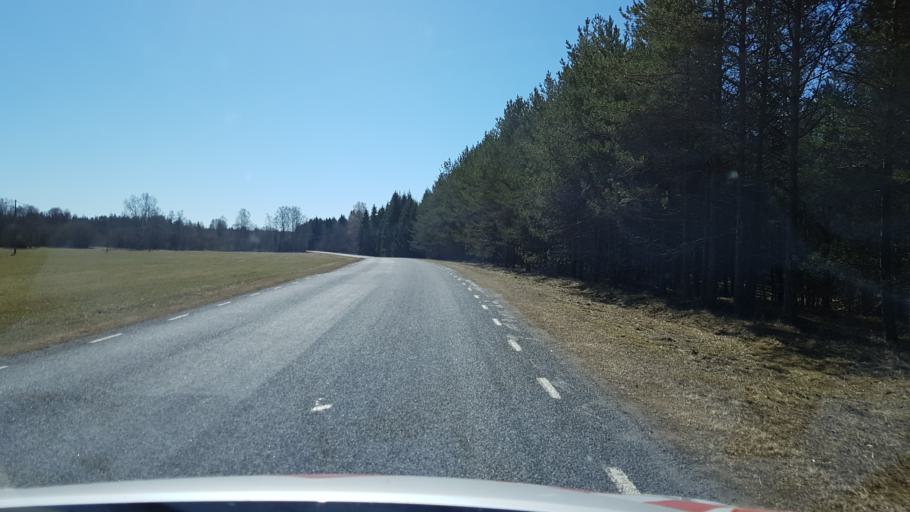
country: EE
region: Laeaene-Virumaa
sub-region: Haljala vald
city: Haljala
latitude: 59.5146
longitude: 26.2307
